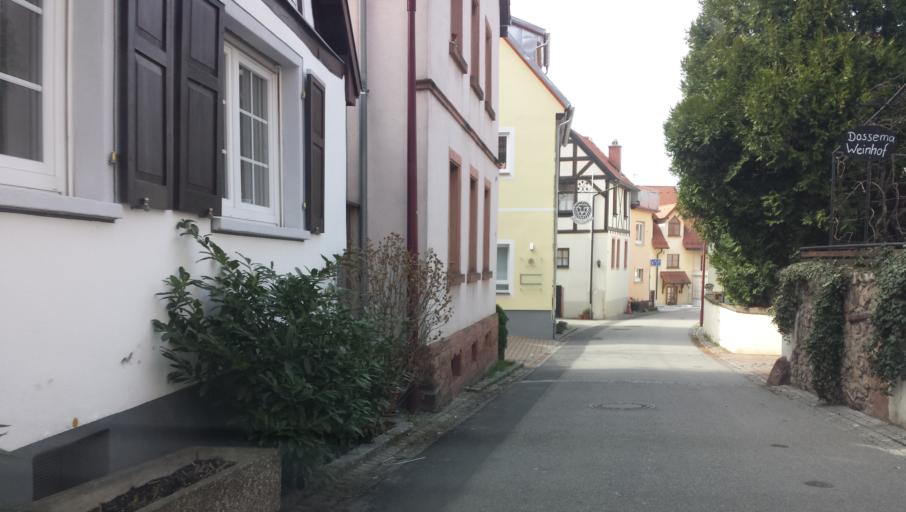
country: DE
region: Baden-Wuerttemberg
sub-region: Karlsruhe Region
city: Dossenheim
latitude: 49.4520
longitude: 8.6775
